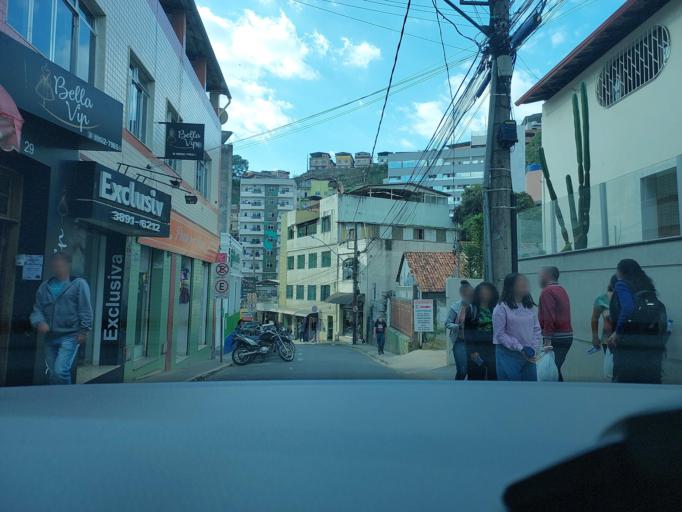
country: BR
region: Minas Gerais
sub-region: Vicosa
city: Vicosa
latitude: -20.7530
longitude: -42.8814
